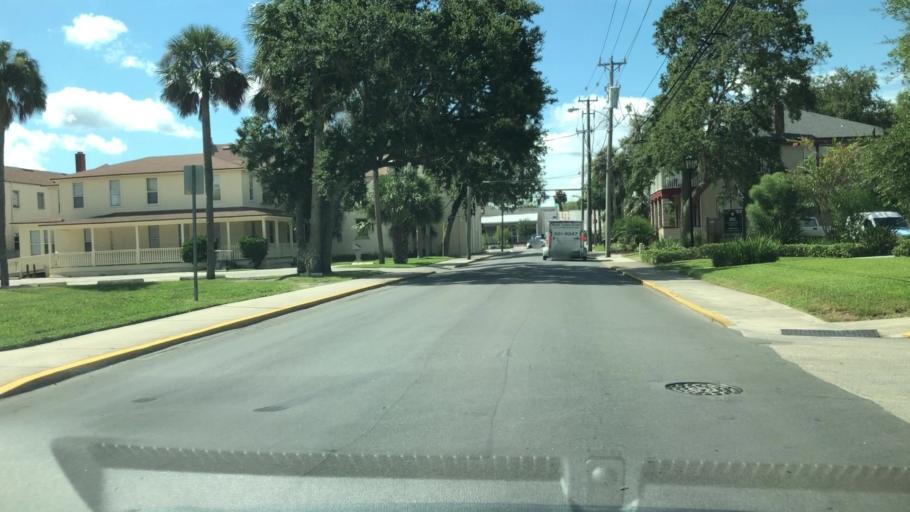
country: US
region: Florida
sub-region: Saint Johns County
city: Saint Augustine
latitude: 29.8925
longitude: -81.3186
